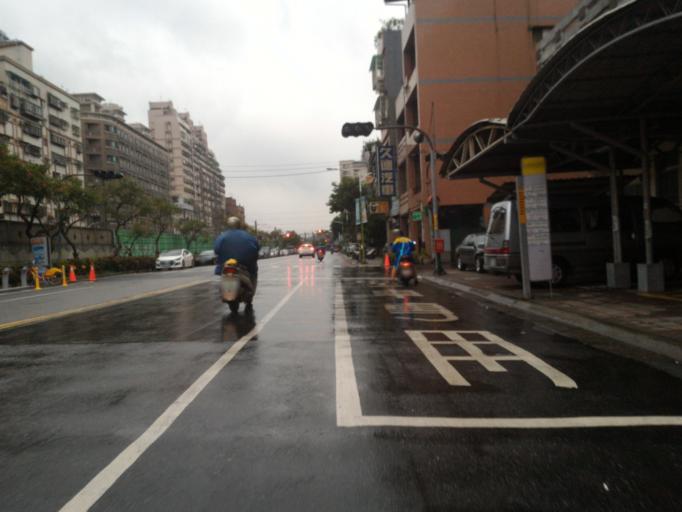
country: TW
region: Taipei
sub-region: Taipei
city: Banqiao
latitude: 24.9841
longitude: 121.4151
